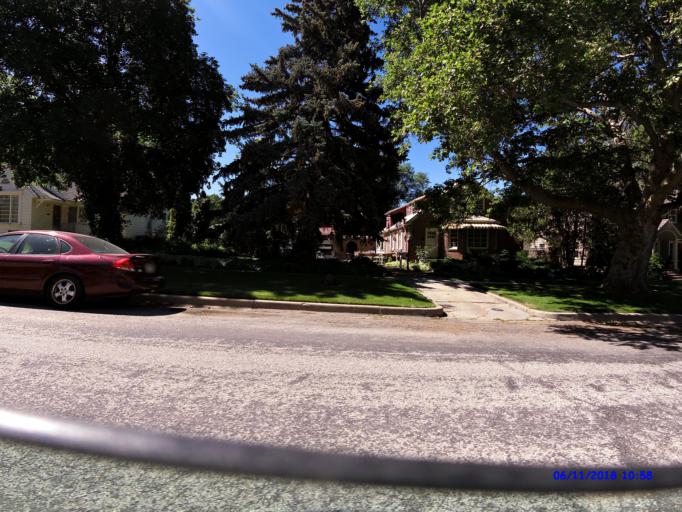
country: US
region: Utah
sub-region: Weber County
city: Ogden
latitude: 41.2162
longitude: -111.9450
